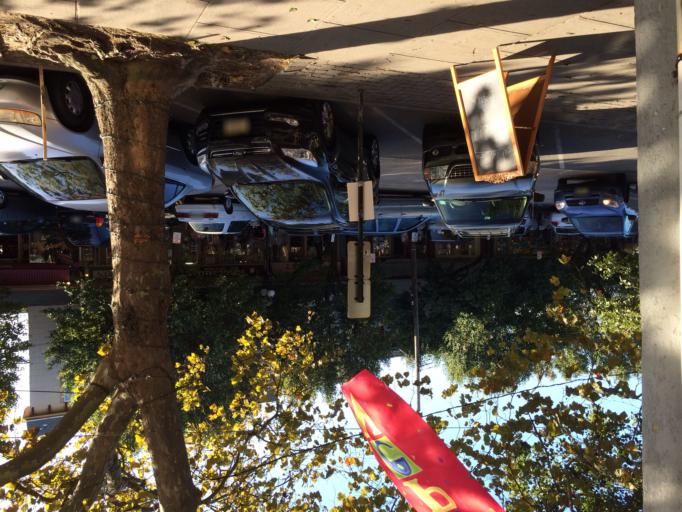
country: US
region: New Jersey
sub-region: Monmouth County
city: Ocean Grove
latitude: 40.2123
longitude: -74.0070
